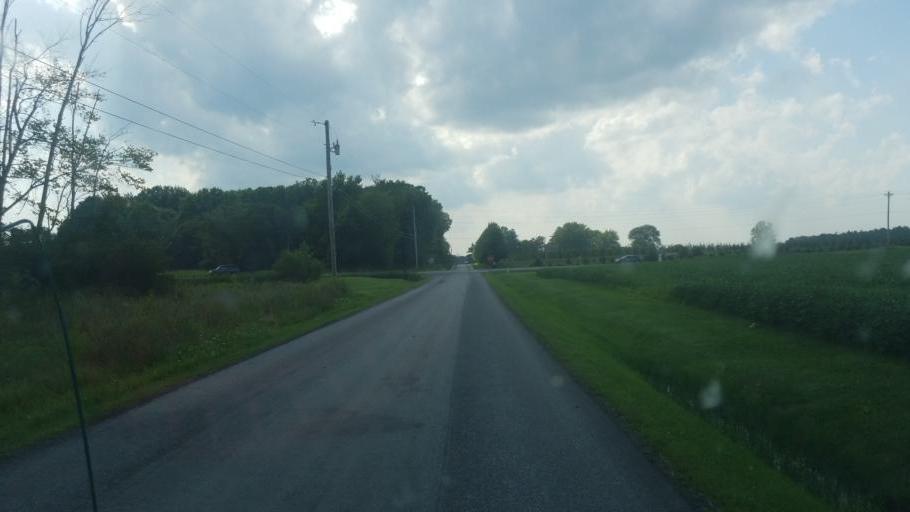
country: US
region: Ohio
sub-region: Wayne County
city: West Salem
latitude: 40.9522
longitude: -82.0831
